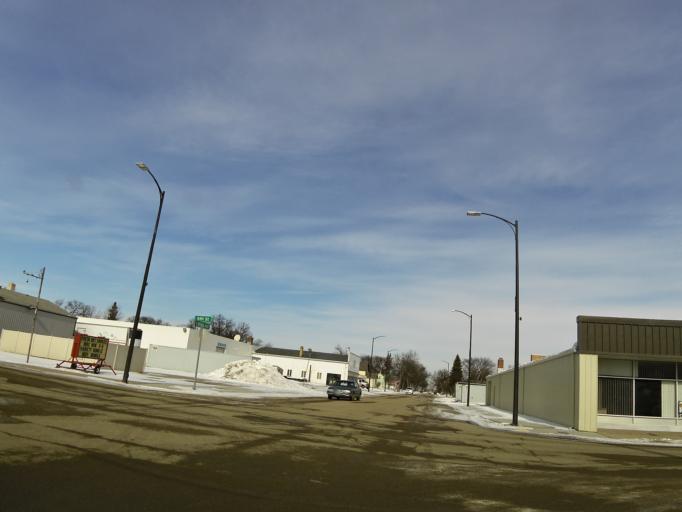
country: US
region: North Dakota
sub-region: Walsh County
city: Grafton
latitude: 48.4195
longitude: -97.4126
